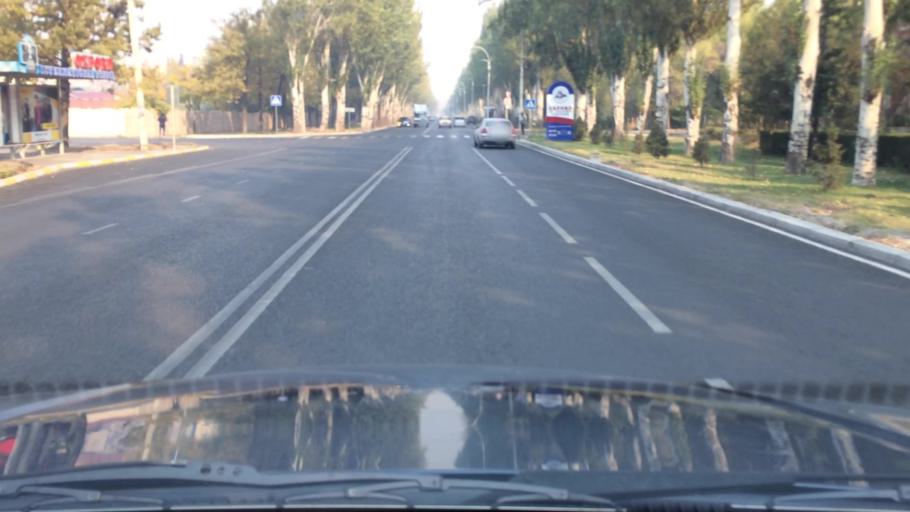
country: KG
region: Chuy
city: Bishkek
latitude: 42.8316
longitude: 74.5853
